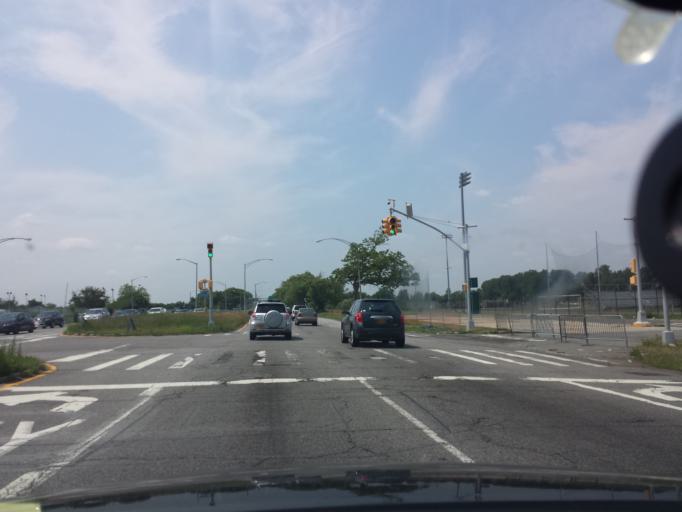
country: US
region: New York
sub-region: Kings County
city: Brooklyn
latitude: 40.5900
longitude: -73.9007
